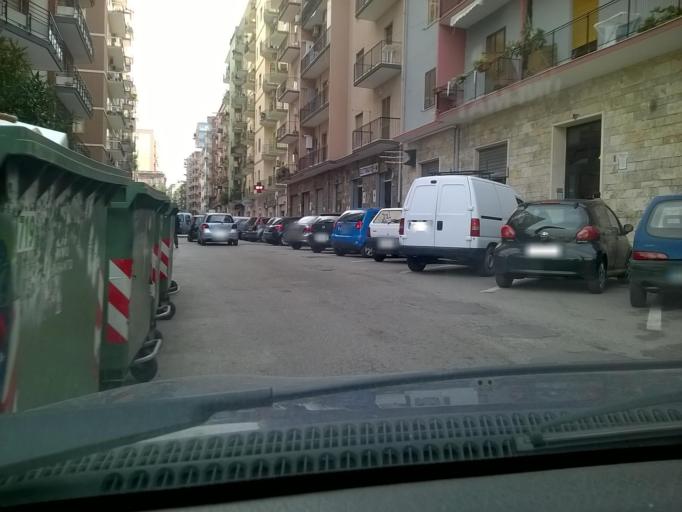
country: IT
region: Apulia
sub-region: Provincia di Taranto
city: Taranto
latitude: 40.4673
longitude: 17.2561
